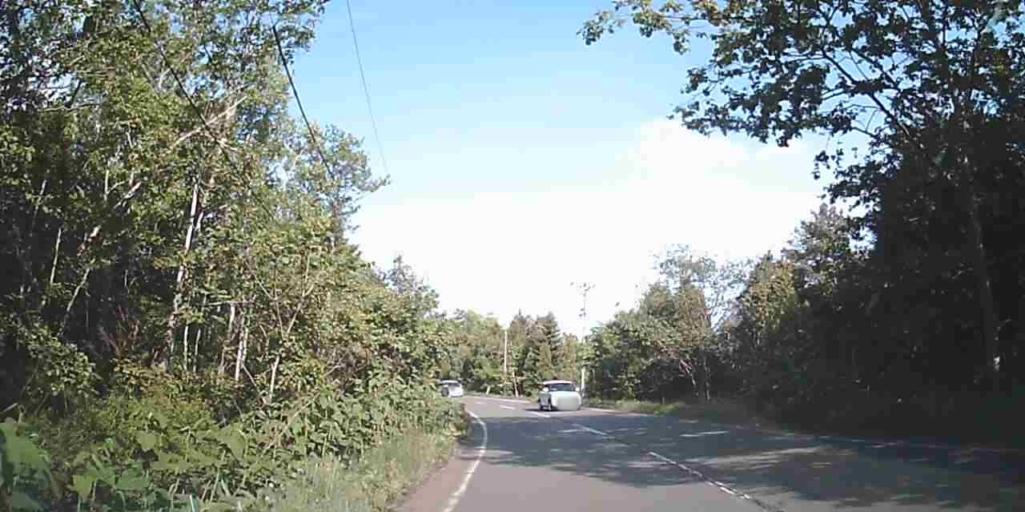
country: JP
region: Hokkaido
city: Tomakomai
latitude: 42.6400
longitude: 141.4786
